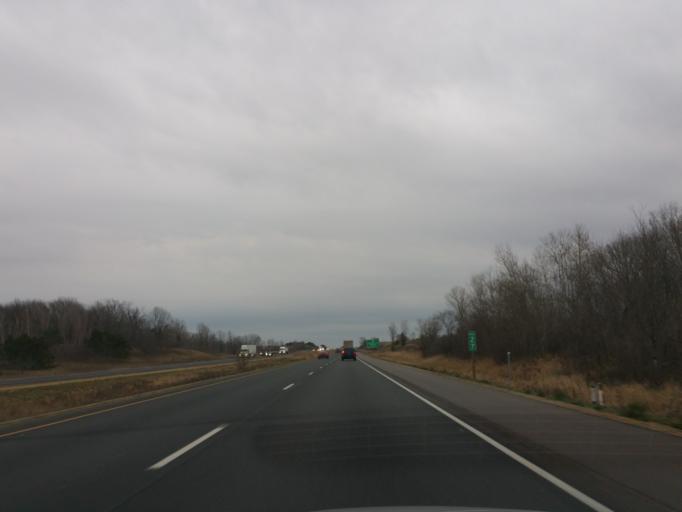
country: US
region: Wisconsin
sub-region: Saint Croix County
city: Woodville
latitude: 44.9337
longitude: -92.2281
